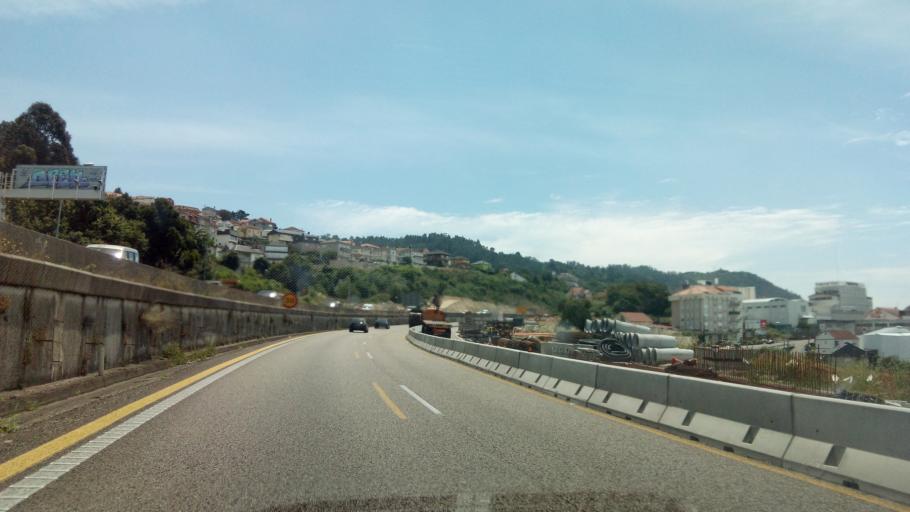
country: ES
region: Galicia
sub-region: Provincia de Pontevedra
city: Redondela
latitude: 42.2708
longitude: -8.6638
